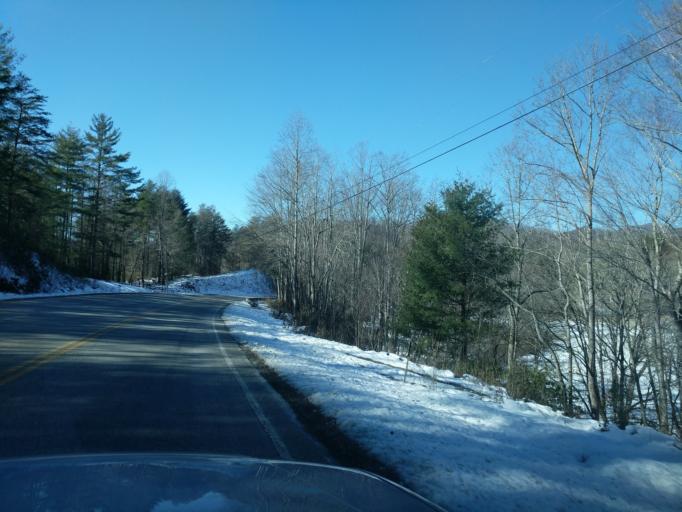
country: US
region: Georgia
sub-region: Towns County
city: Hiawassee
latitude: 34.9252
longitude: -83.6277
